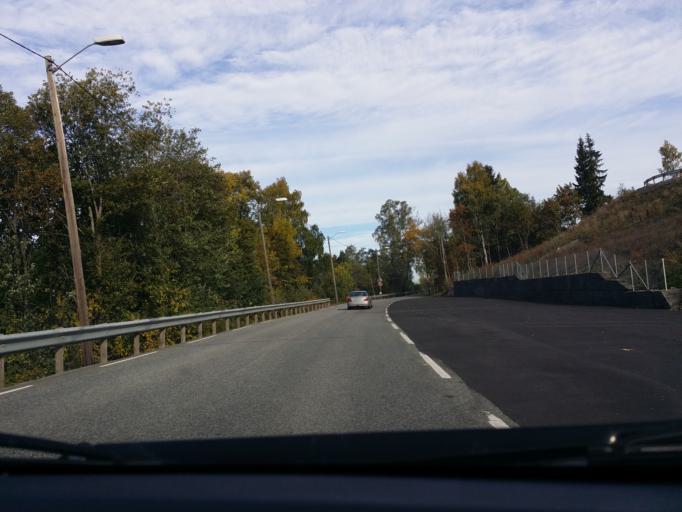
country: NO
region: Buskerud
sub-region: Lier
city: Tranby
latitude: 59.8303
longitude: 10.2561
